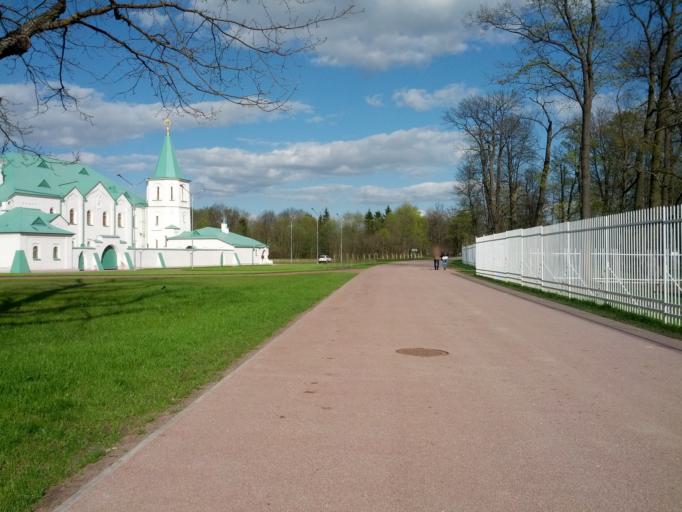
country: RU
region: St.-Petersburg
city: Pushkin
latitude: 59.7250
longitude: 30.3845
